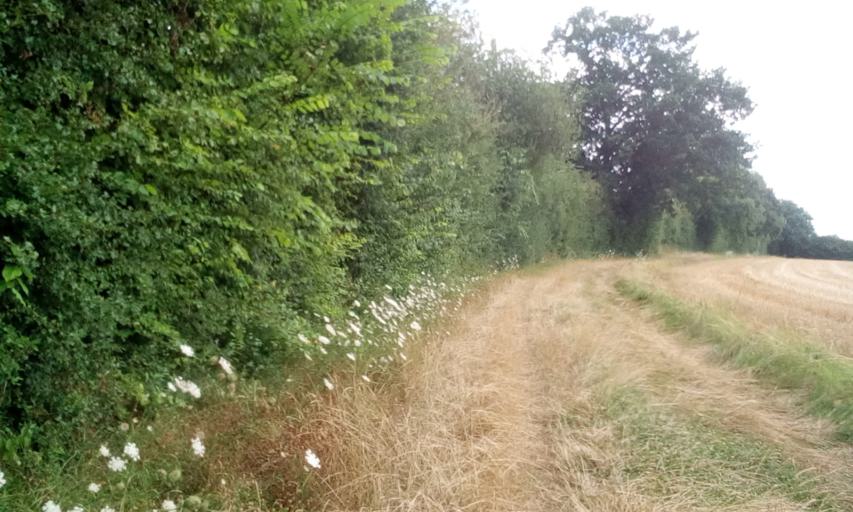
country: FR
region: Lower Normandy
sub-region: Departement du Calvados
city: Troarn
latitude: 49.1659
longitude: -0.1902
